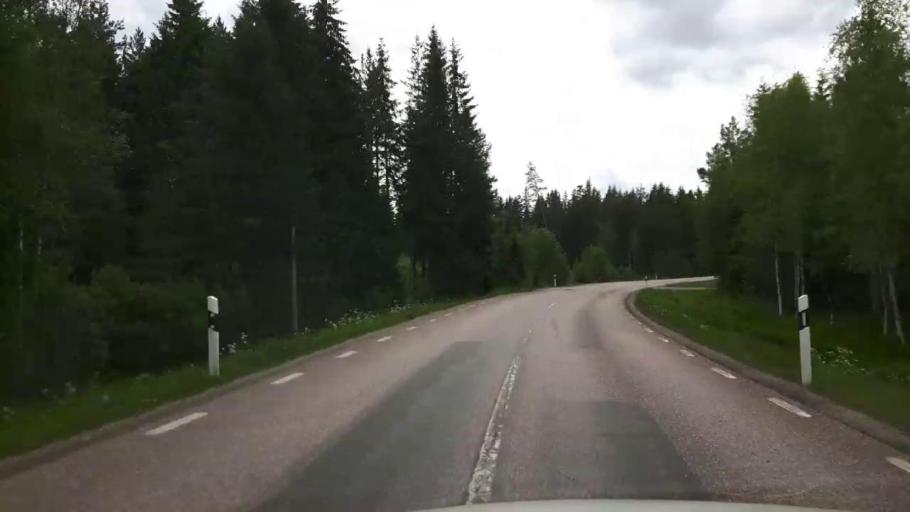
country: SE
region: Dalarna
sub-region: Hedemora Kommun
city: Brunna
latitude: 60.1689
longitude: 15.9961
